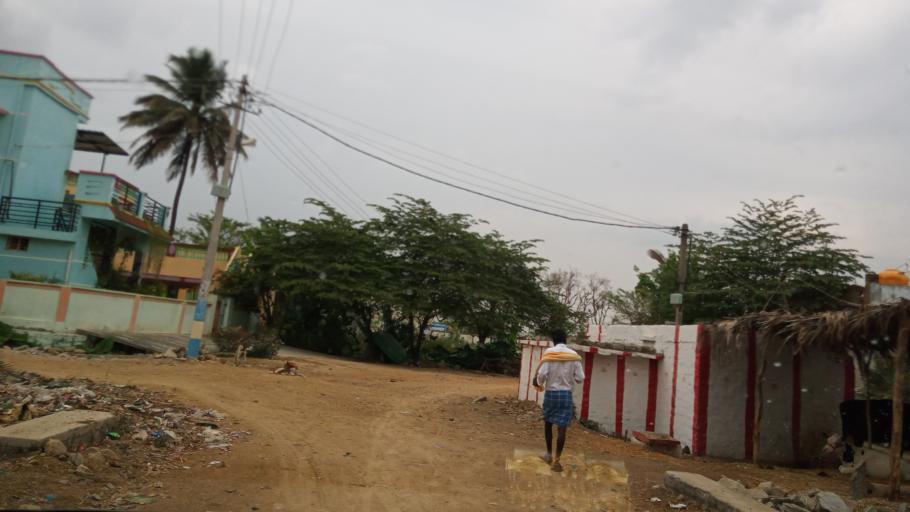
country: IN
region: Karnataka
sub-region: Kolar
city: Mulbagal
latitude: 13.1079
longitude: 78.3292
